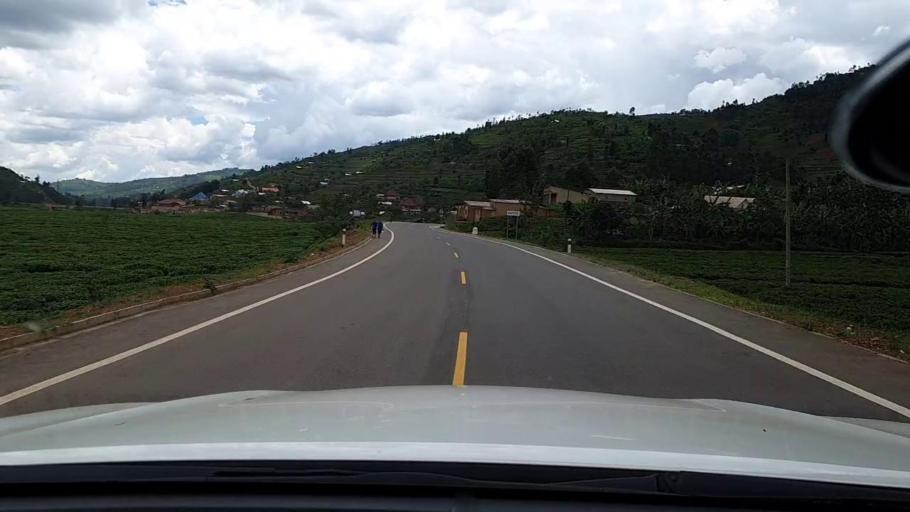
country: RW
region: Northern Province
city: Byumba
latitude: -1.6503
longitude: 29.9024
